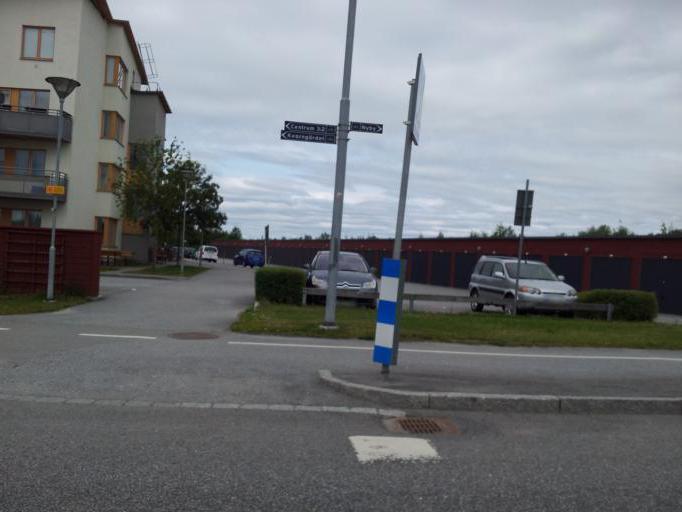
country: SE
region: Uppsala
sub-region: Uppsala Kommun
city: Gamla Uppsala
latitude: 59.8829
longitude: 17.6554
